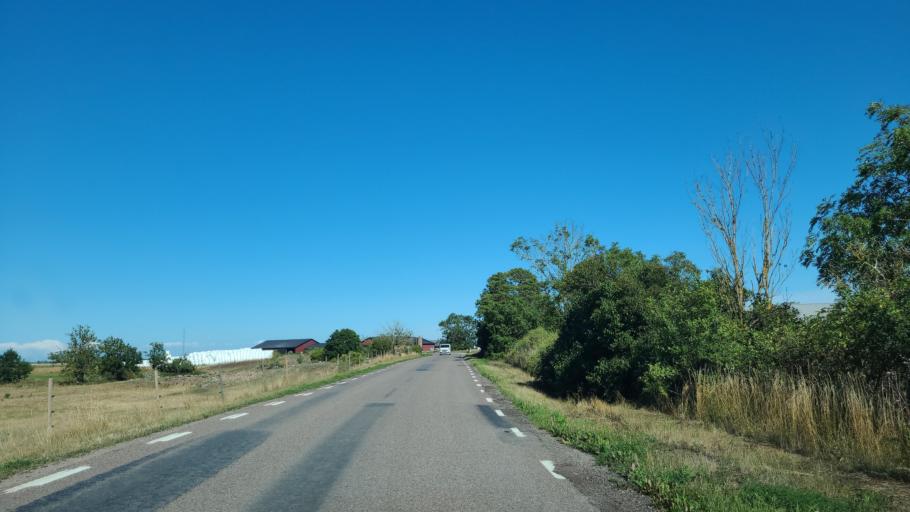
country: SE
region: Kalmar
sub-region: Borgholms Kommun
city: Borgholm
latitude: 56.8598
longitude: 16.8172
